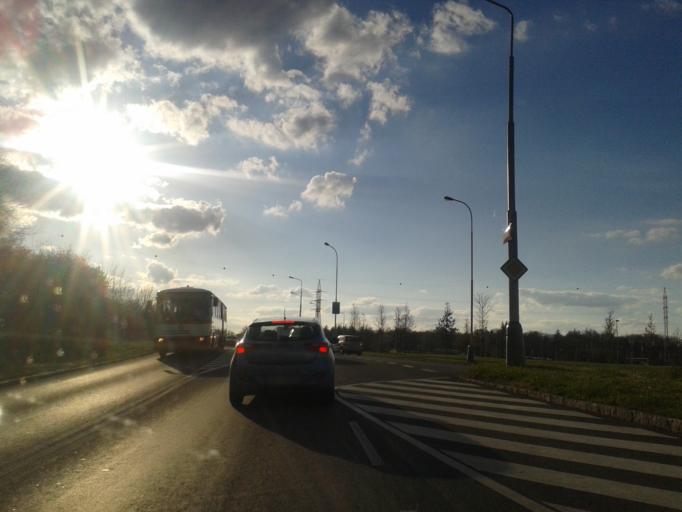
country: CZ
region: Central Bohemia
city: Horomerice
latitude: 50.0778
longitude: 14.3475
